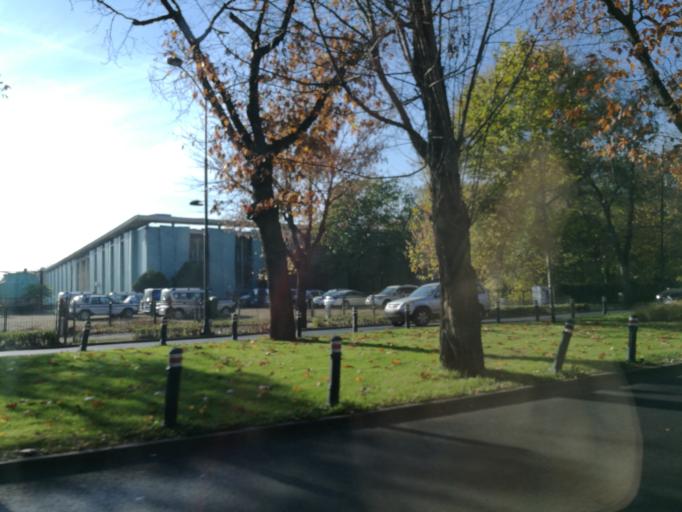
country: RO
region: Bucuresti
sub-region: Municipiul Bucuresti
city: Bucharest
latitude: 44.4627
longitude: 26.0925
